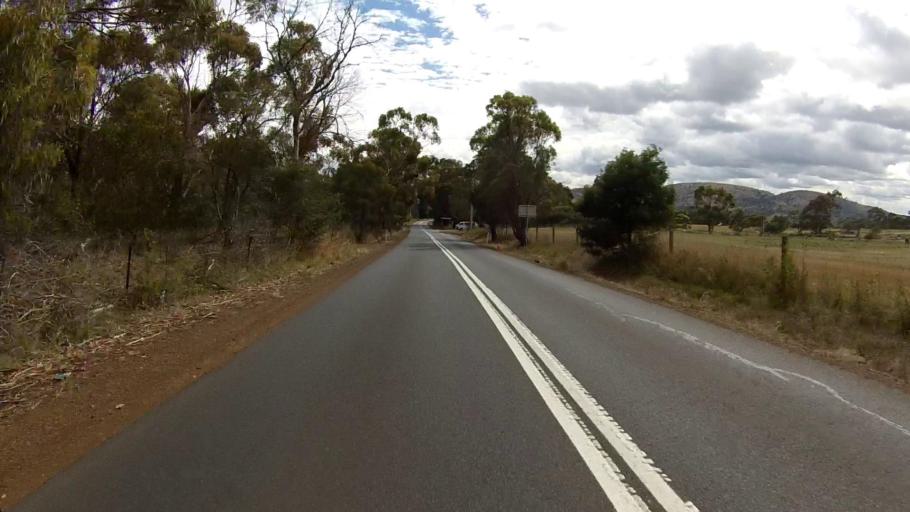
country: AU
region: Tasmania
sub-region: Clarence
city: Lindisfarne
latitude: -42.7661
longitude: 147.3921
